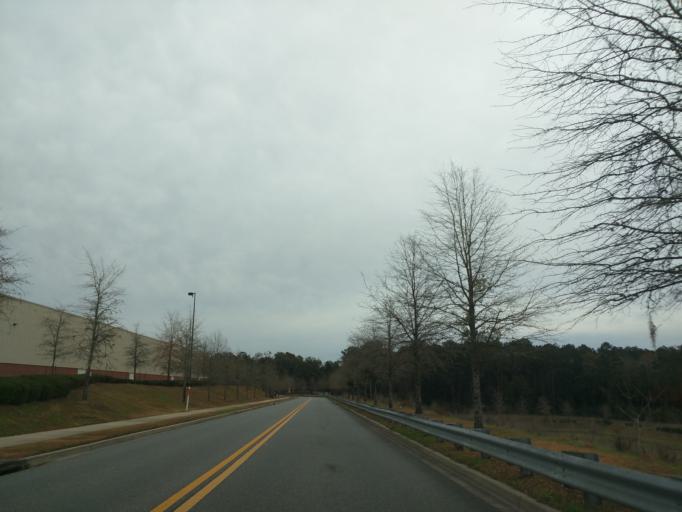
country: US
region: Florida
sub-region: Leon County
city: Tallahassee
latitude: 30.4597
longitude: -84.2133
